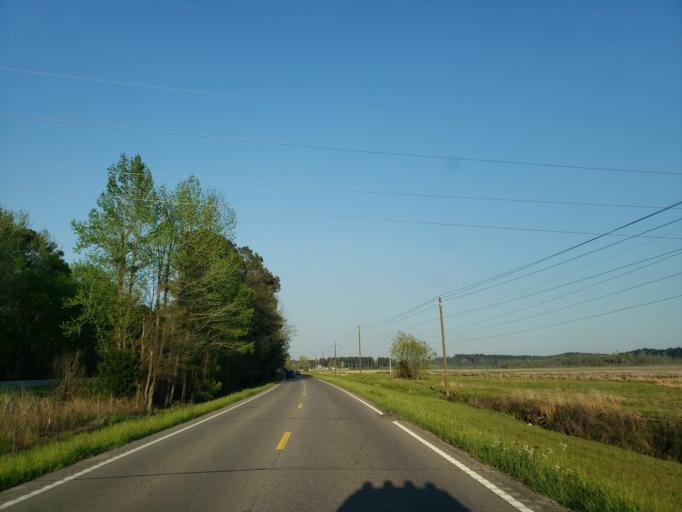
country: US
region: Mississippi
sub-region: Lauderdale County
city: Marion
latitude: 32.3942
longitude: -88.6282
